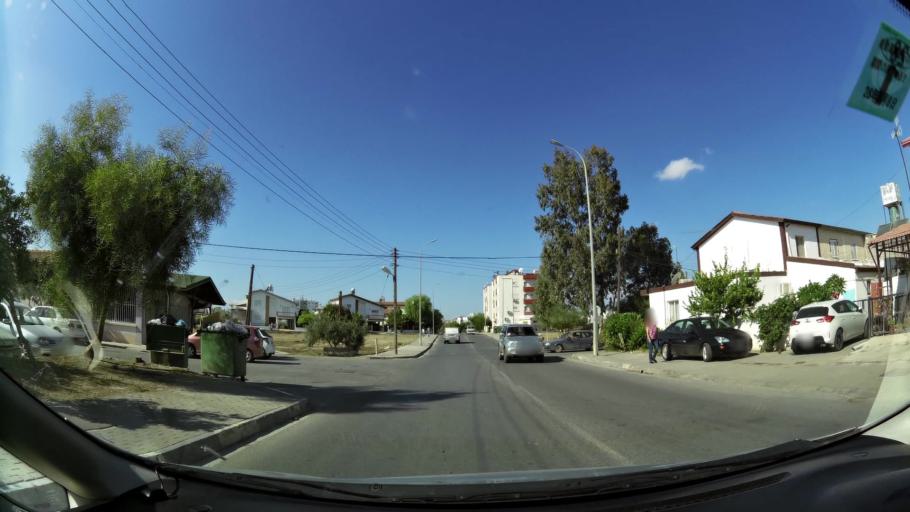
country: CY
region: Lefkosia
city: Nicosia
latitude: 35.2061
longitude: 33.3363
